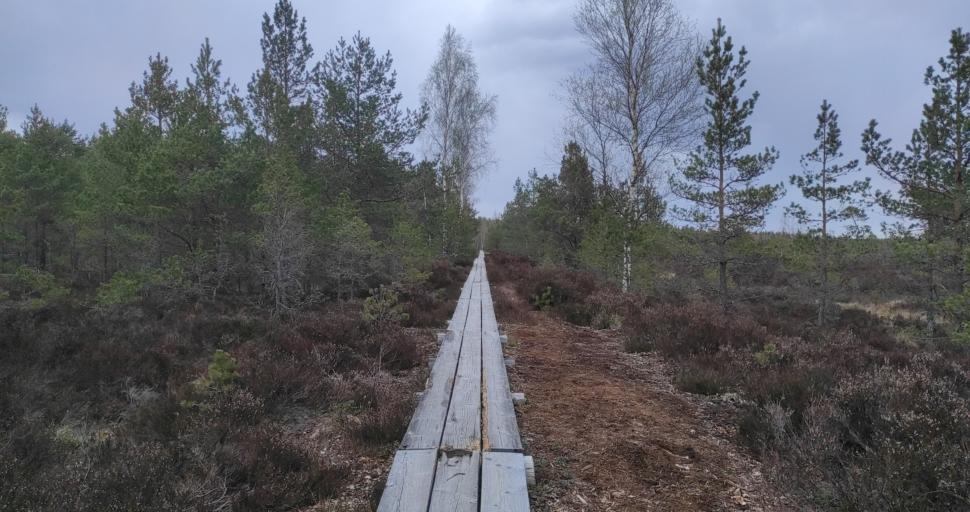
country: LV
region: Dundaga
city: Dundaga
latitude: 57.3506
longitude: 22.1501
